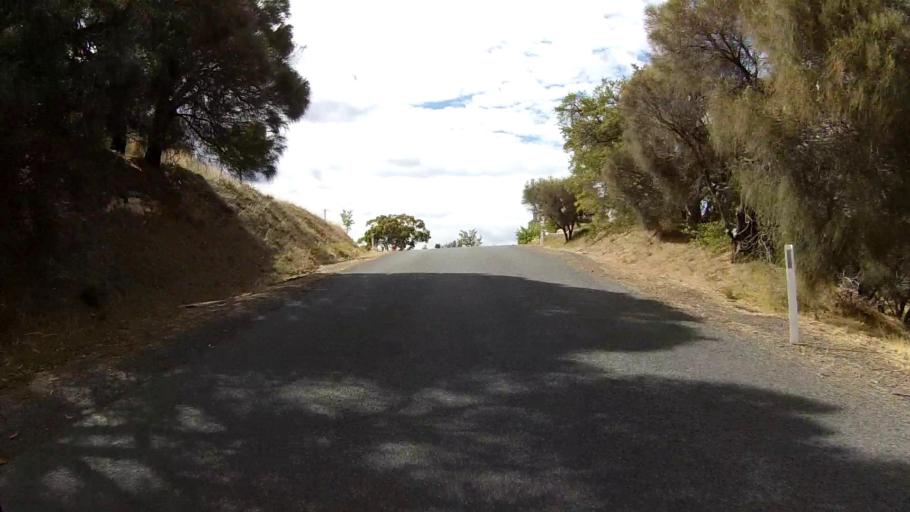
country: AU
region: Tasmania
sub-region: Glenorchy
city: Goodwood
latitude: -42.8103
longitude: 147.3014
